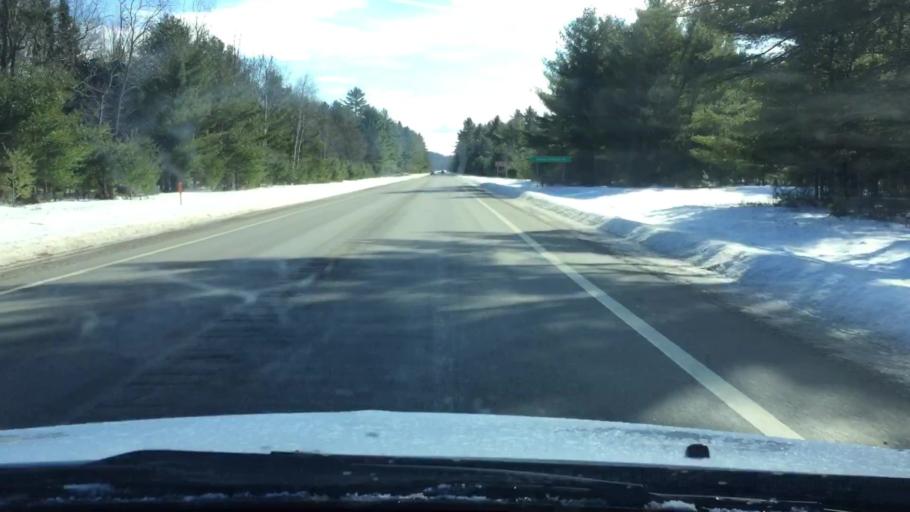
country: US
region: Michigan
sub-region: Charlevoix County
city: East Jordan
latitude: 45.0363
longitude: -85.0678
